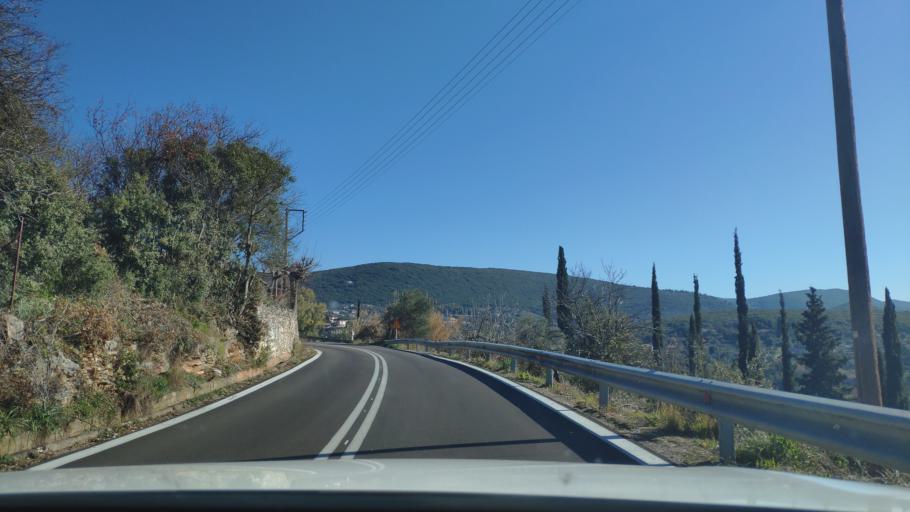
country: GR
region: West Greece
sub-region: Nomos Aitolias kai Akarnanias
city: Thermo
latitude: 38.5833
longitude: 21.6322
